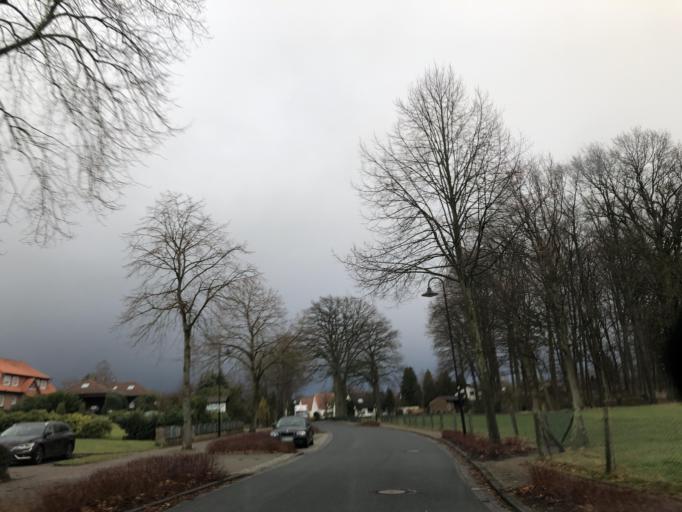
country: DE
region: Lower Saxony
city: Bad Fallingbostel
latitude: 52.8776
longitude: 9.7061
